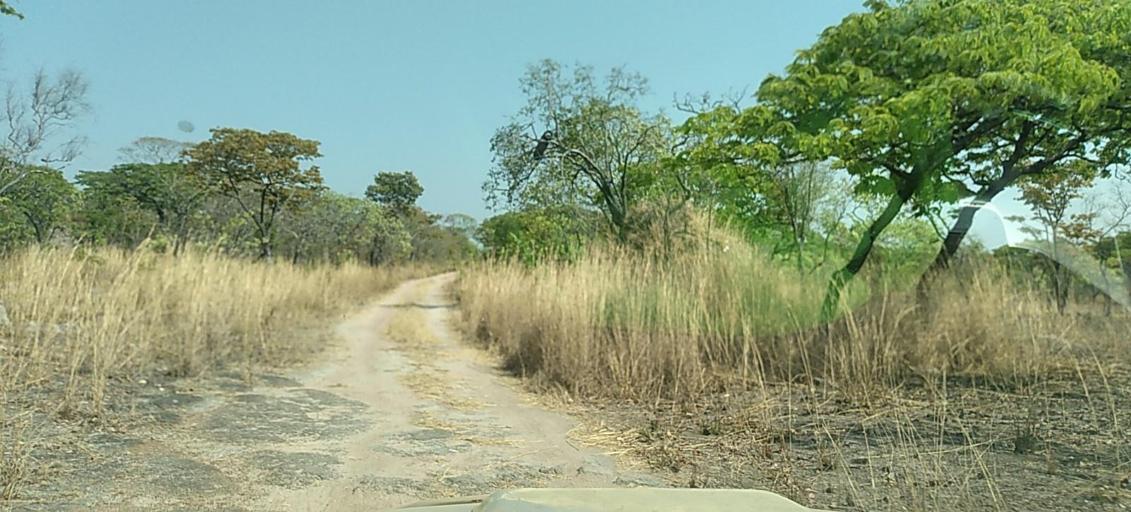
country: ZM
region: North-Western
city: Kalengwa
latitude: -13.3260
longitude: 24.8284
